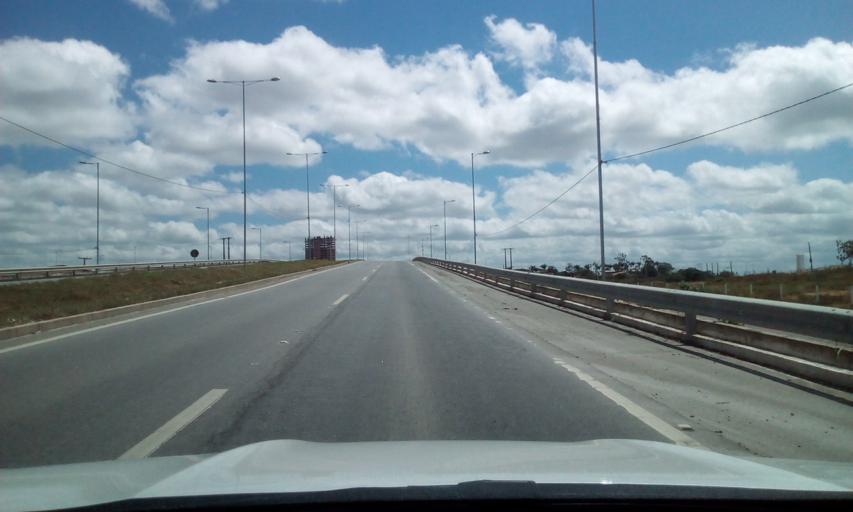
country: BR
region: Paraiba
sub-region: Campina Grande
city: Campina Grande
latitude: -7.2581
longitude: -35.8774
